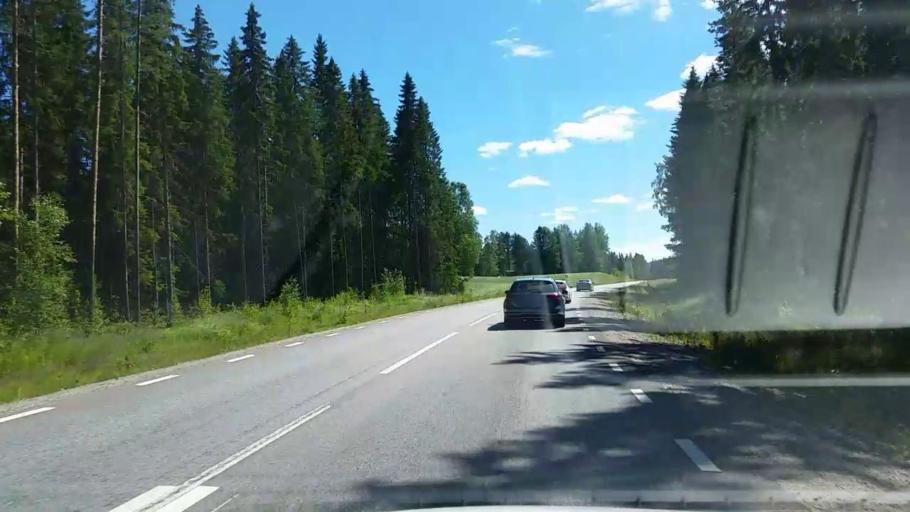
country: SE
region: Gaevleborg
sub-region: Ovanakers Kommun
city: Edsbyn
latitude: 61.2013
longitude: 15.8736
